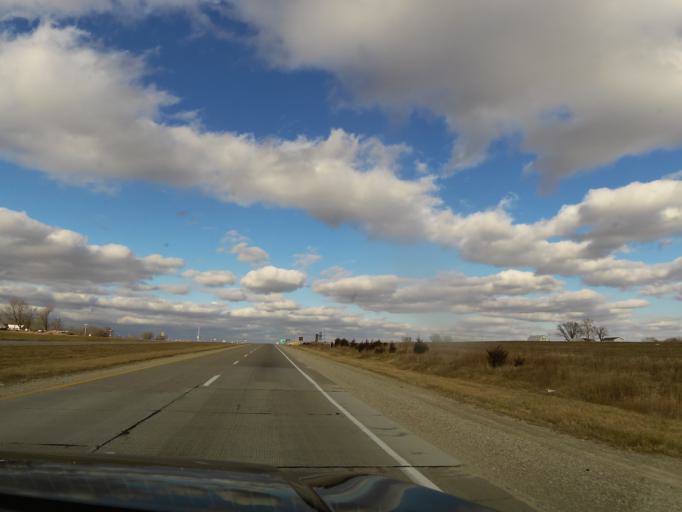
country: US
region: Illinois
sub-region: Hancock County
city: Nauvoo
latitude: 40.5872
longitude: -91.5639
